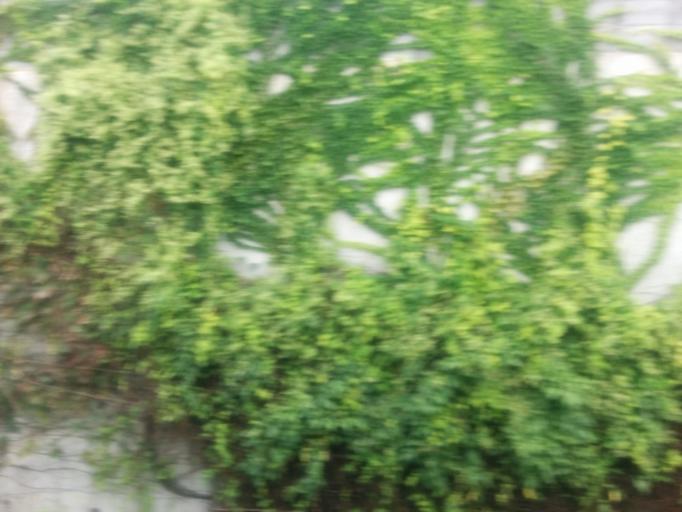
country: JP
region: Kyoto
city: Uji
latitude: 34.9364
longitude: 135.7677
